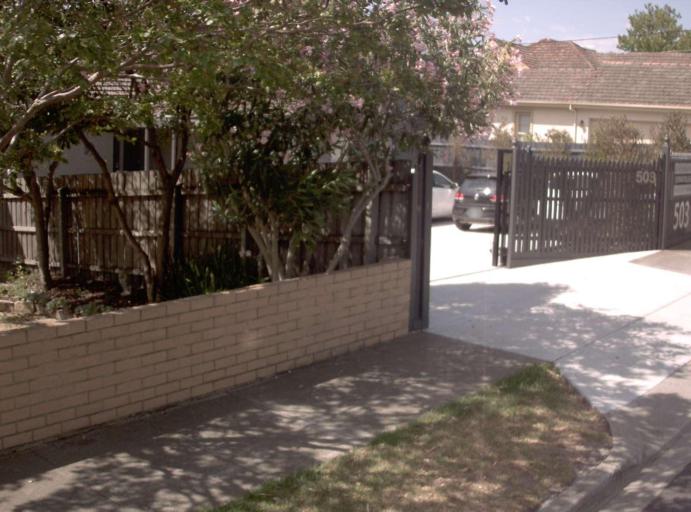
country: AU
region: Victoria
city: Carnegie
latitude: -37.8794
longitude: 145.0754
